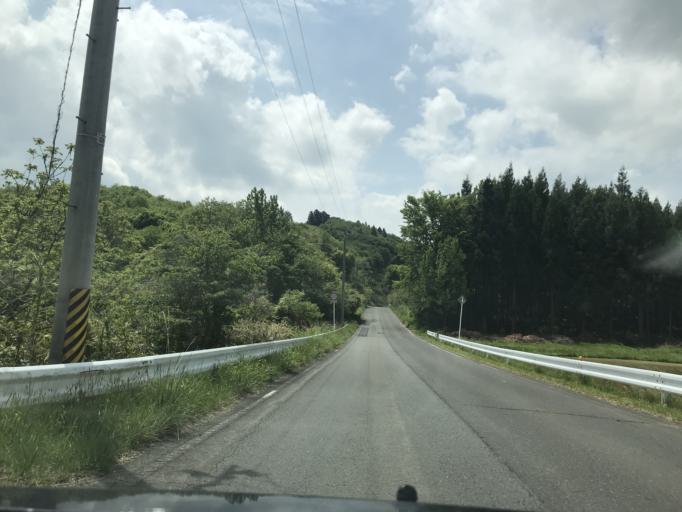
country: JP
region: Miyagi
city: Furukawa
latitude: 38.7577
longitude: 140.9391
